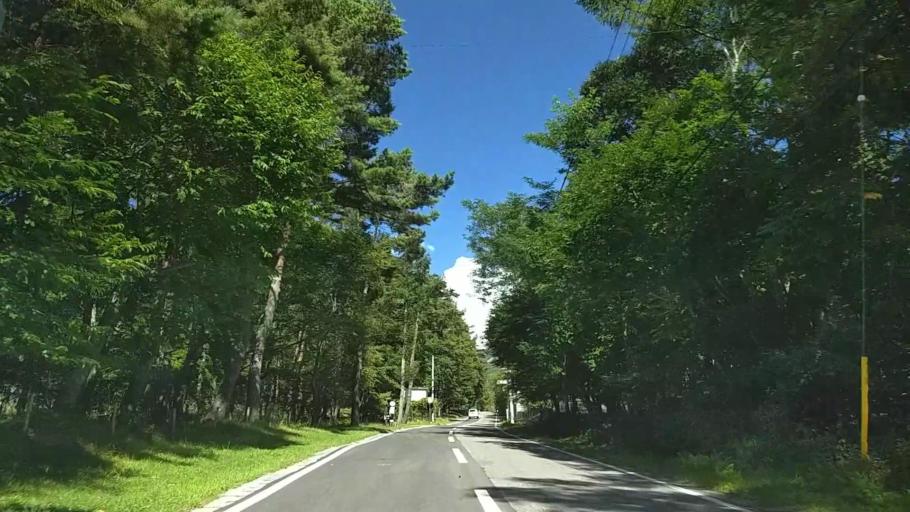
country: JP
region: Nagano
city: Chino
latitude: 36.0612
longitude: 138.2760
